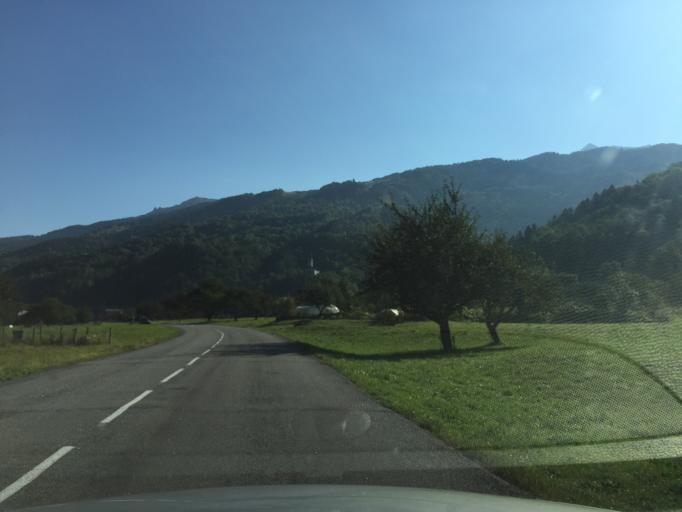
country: FR
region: Rhone-Alpes
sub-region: Departement de la Savoie
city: Bourg-Saint-Maurice
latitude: 45.5692
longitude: 6.7328
